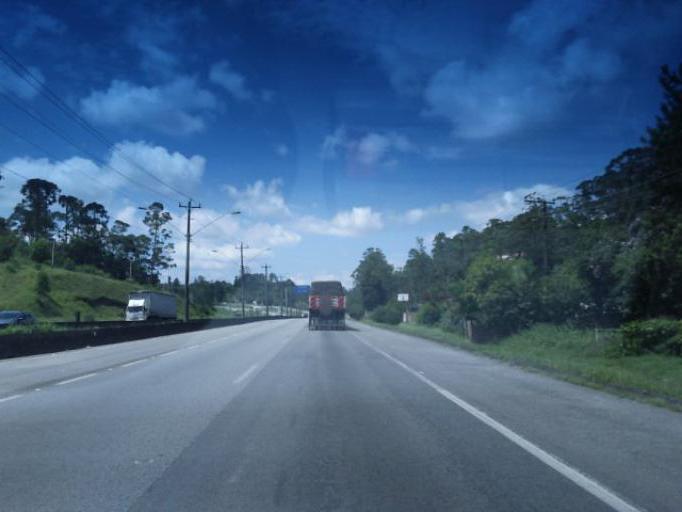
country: BR
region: Sao Paulo
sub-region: Sao Lourenco Da Serra
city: Sao Lourenco da Serra
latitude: -23.7737
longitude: -46.9137
